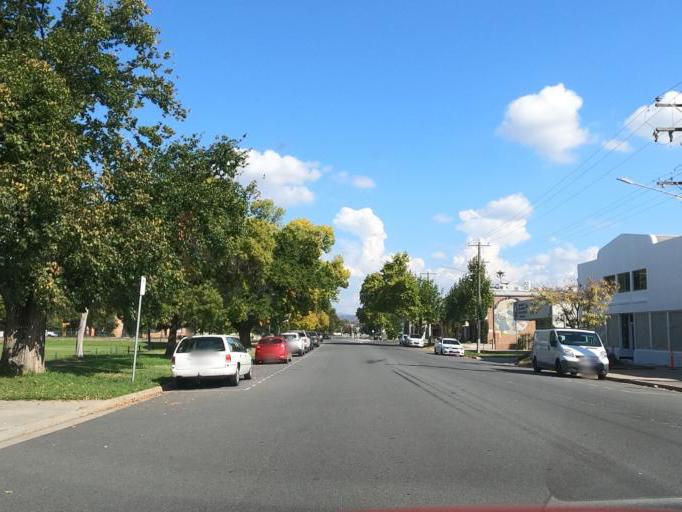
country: AU
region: New South Wales
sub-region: Albury Municipality
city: South Albury
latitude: -36.0855
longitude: 146.9123
